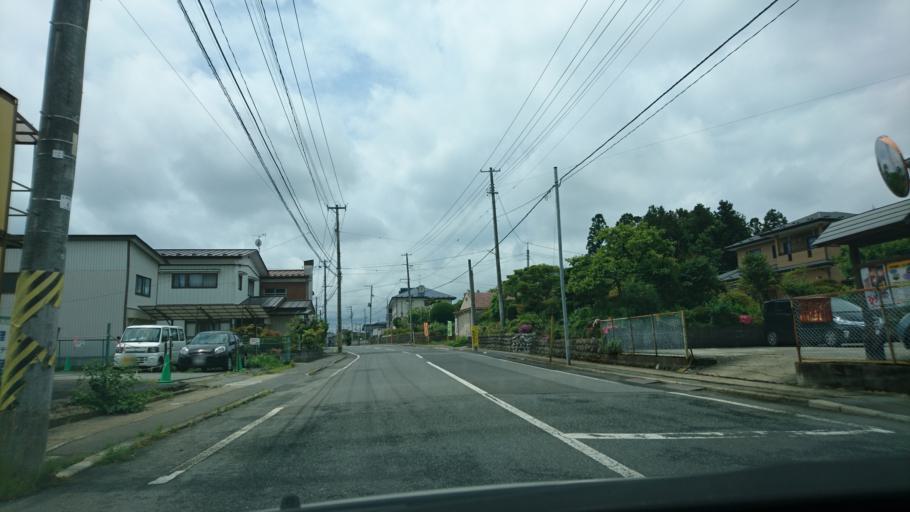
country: JP
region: Iwate
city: Ichinoseki
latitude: 38.9282
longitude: 141.1247
